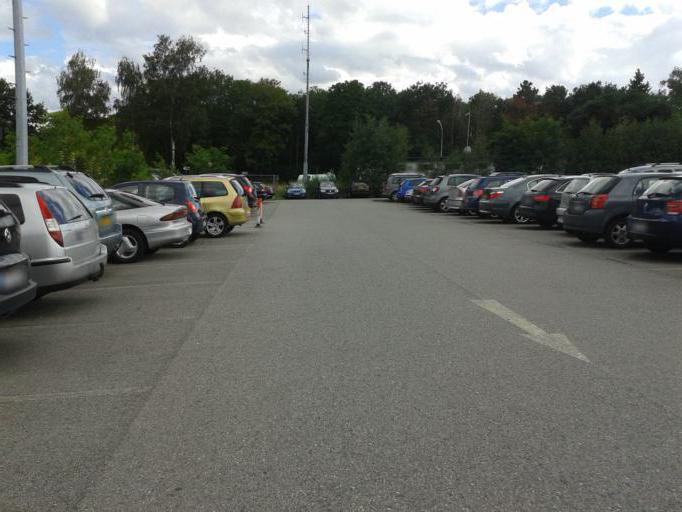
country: DE
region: North Rhine-Westphalia
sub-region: Regierungsbezirk Dusseldorf
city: Weeze
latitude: 51.5973
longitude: 6.1473
